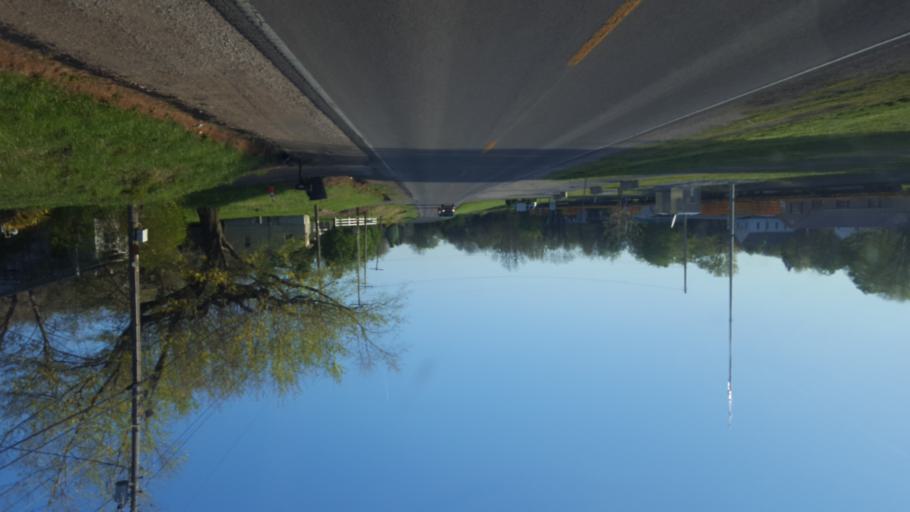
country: US
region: Kentucky
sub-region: Hart County
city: Munfordville
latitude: 37.2383
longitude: -85.8921
